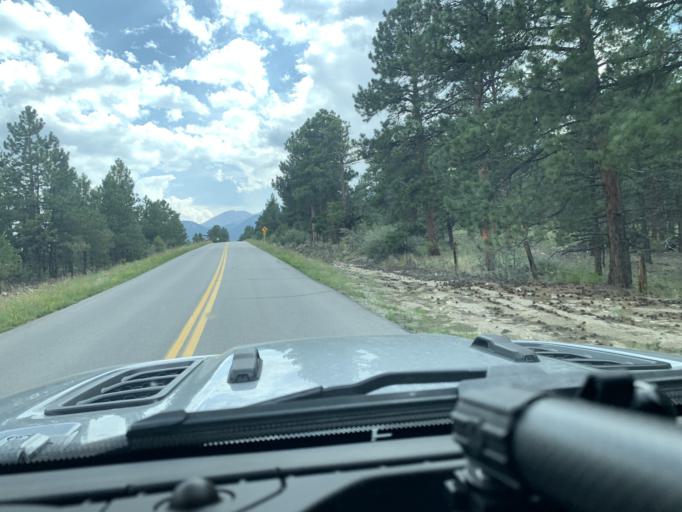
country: US
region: Colorado
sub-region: Chaffee County
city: Buena Vista
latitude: 38.7449
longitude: -106.1610
